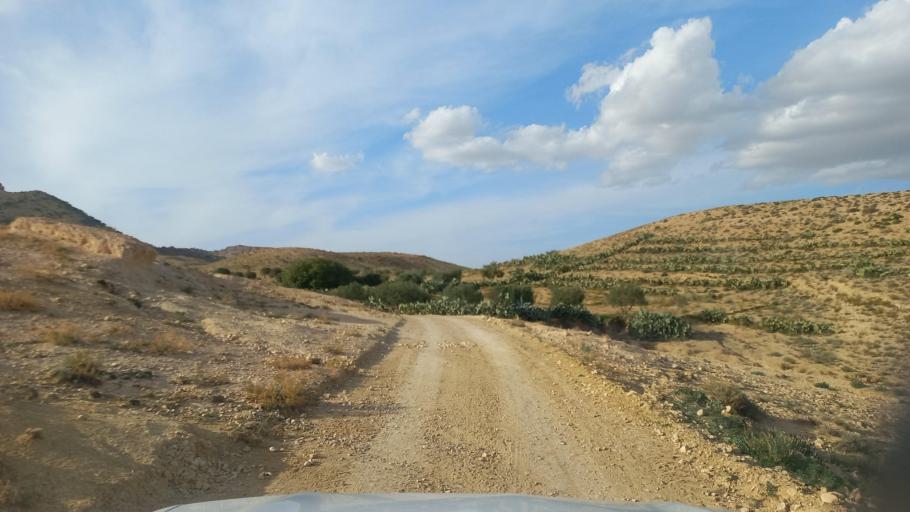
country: TN
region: Al Qasrayn
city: Sbiba
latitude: 35.4569
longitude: 9.0829
